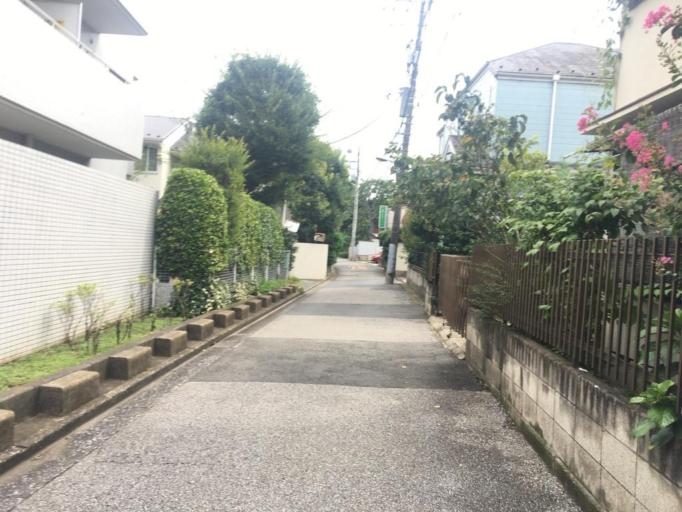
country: JP
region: Tokyo
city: Tokyo
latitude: 35.7199
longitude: 139.6932
